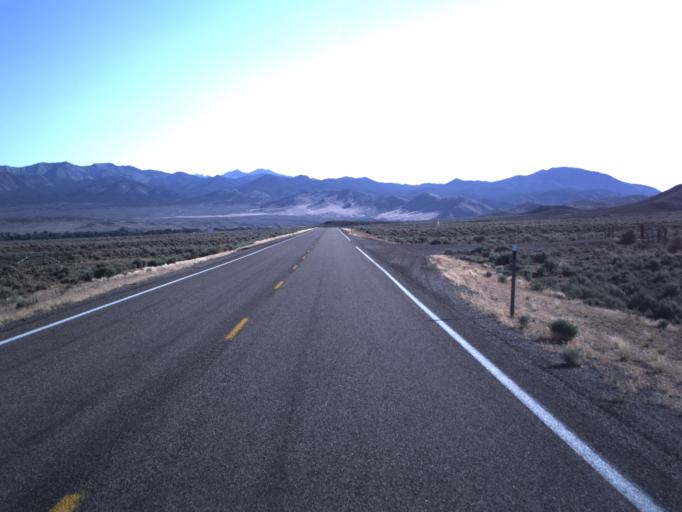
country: US
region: Utah
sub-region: Beaver County
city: Milford
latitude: 38.1824
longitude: -112.9438
